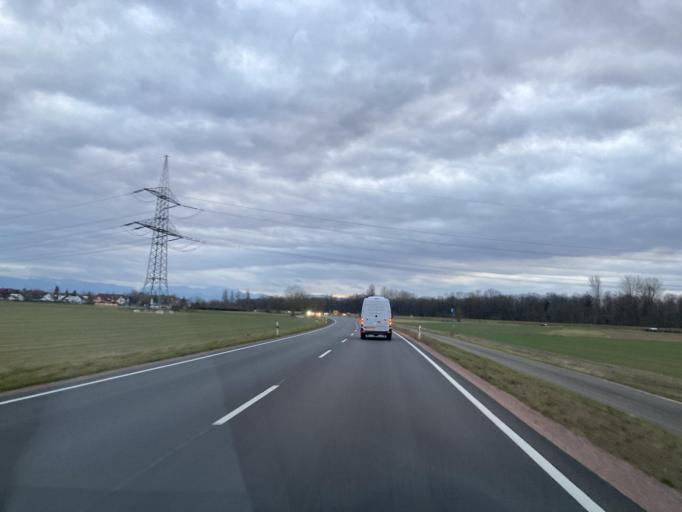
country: DE
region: Baden-Wuerttemberg
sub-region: Freiburg Region
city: Breisach am Rhein
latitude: 48.0231
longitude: 7.6020
